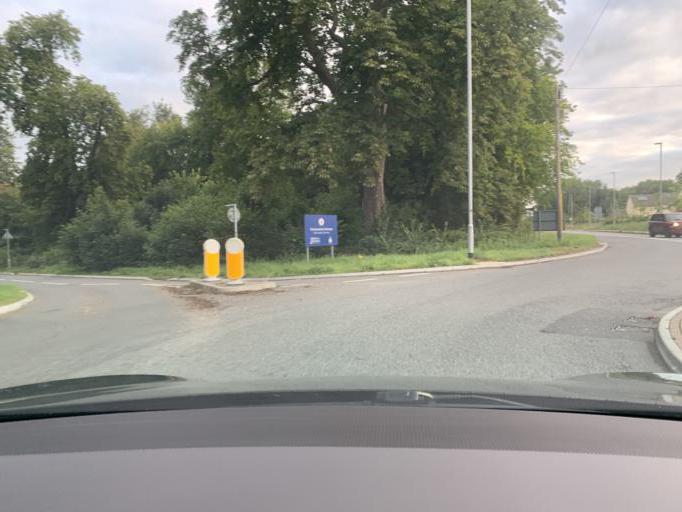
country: GB
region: England
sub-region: Wiltshire
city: Tidworth
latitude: 51.2268
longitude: -1.6640
